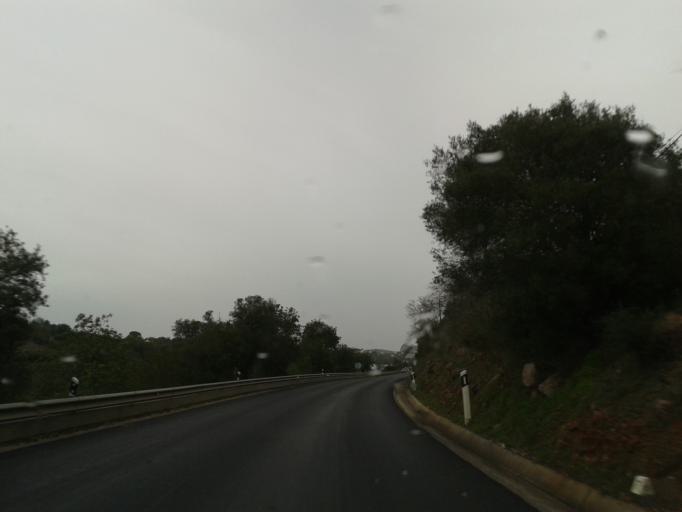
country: PT
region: Faro
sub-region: Silves
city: Silves
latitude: 37.2202
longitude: -8.3646
